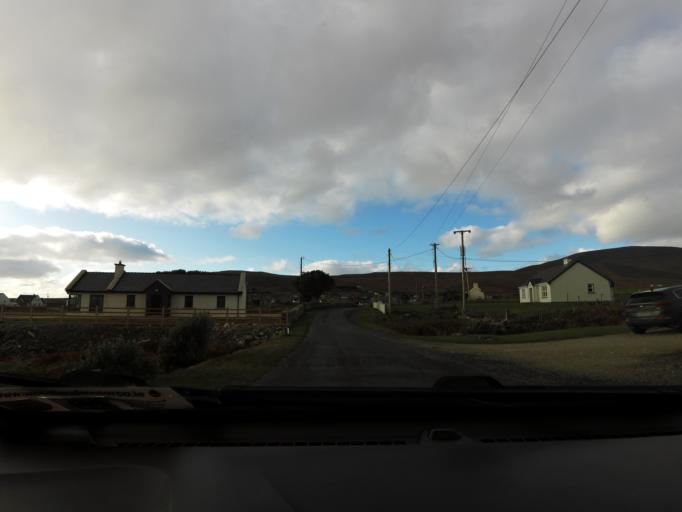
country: IE
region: Connaught
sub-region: Maigh Eo
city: Belmullet
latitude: 53.9215
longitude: -10.0187
